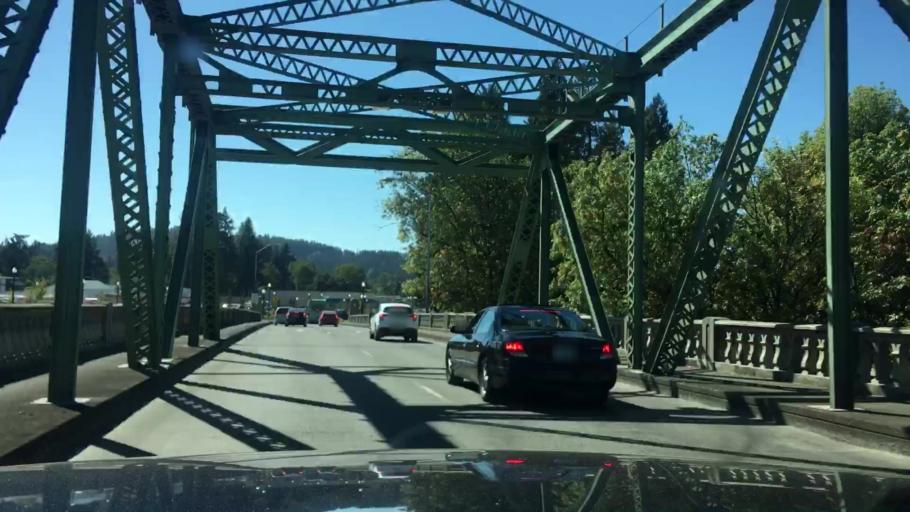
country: US
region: Oregon
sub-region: Lane County
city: Springfield
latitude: 44.0452
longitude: -123.0282
